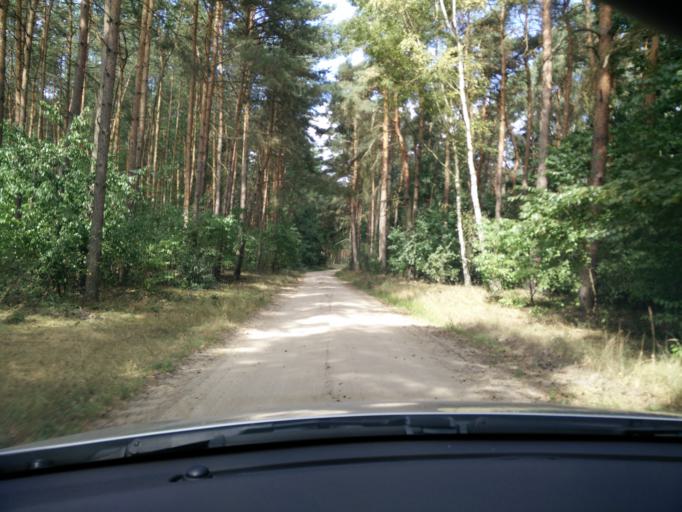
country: PL
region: Greater Poland Voivodeship
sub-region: Powiat sredzki
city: Sroda Wielkopolska
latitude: 52.2812
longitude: 17.2444
